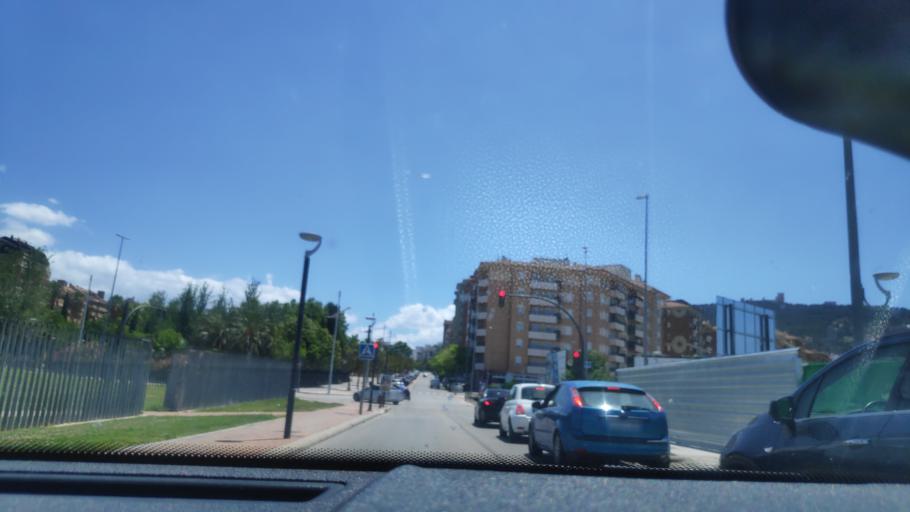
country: ES
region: Andalusia
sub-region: Provincia de Jaen
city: Jaen
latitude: 37.7845
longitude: -3.7913
